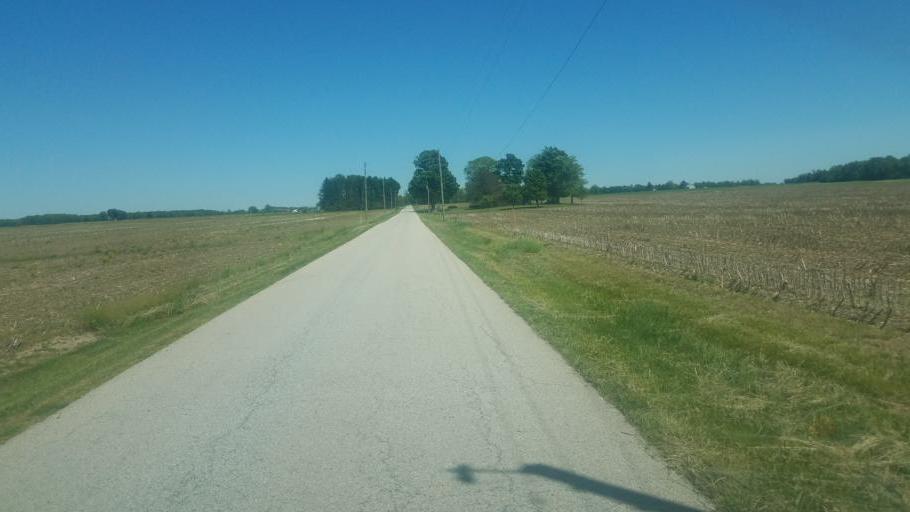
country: US
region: Ohio
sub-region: Champaign County
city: Saint Paris
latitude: 40.1996
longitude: -84.0480
